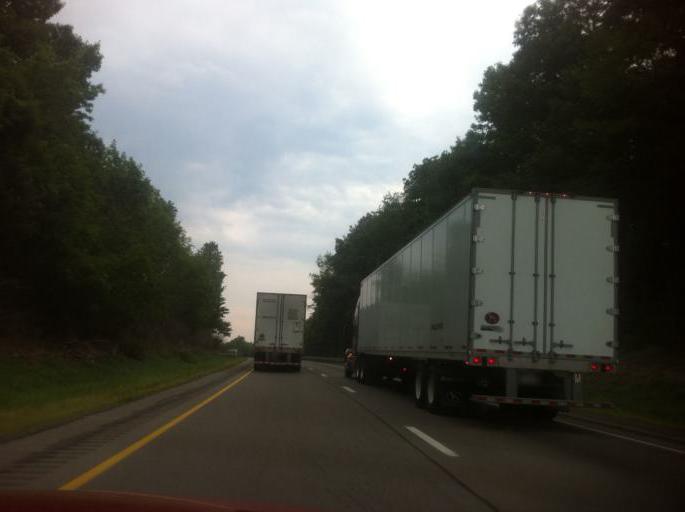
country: US
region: Pennsylvania
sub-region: Jefferson County
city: Brookville
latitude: 41.1877
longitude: -79.1800
